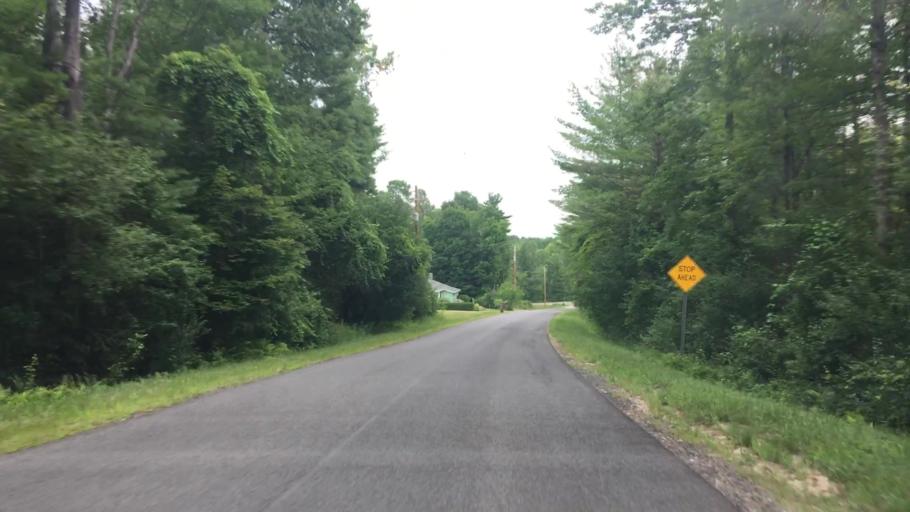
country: US
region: New York
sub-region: Clinton County
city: Peru
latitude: 44.6039
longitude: -73.5892
